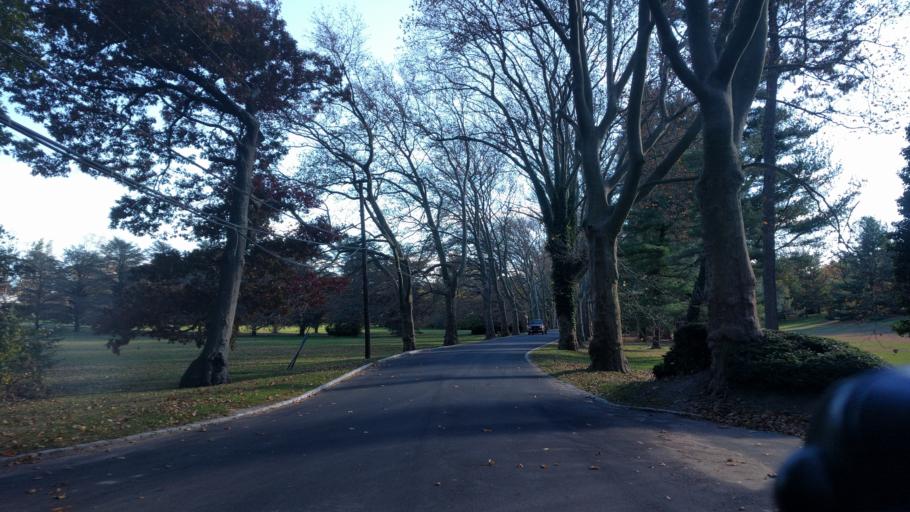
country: US
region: New York
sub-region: Nassau County
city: Bayville
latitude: 40.8906
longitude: -73.5557
